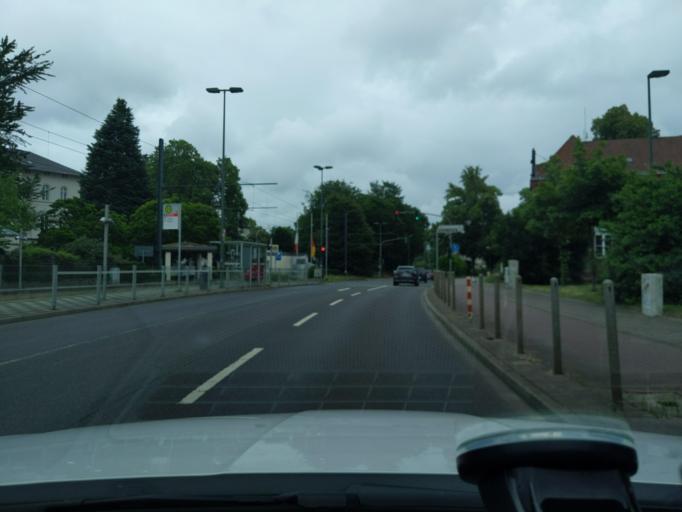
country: DE
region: North Rhine-Westphalia
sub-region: Regierungsbezirk Dusseldorf
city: Ratingen
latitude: 51.2411
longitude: 6.8442
